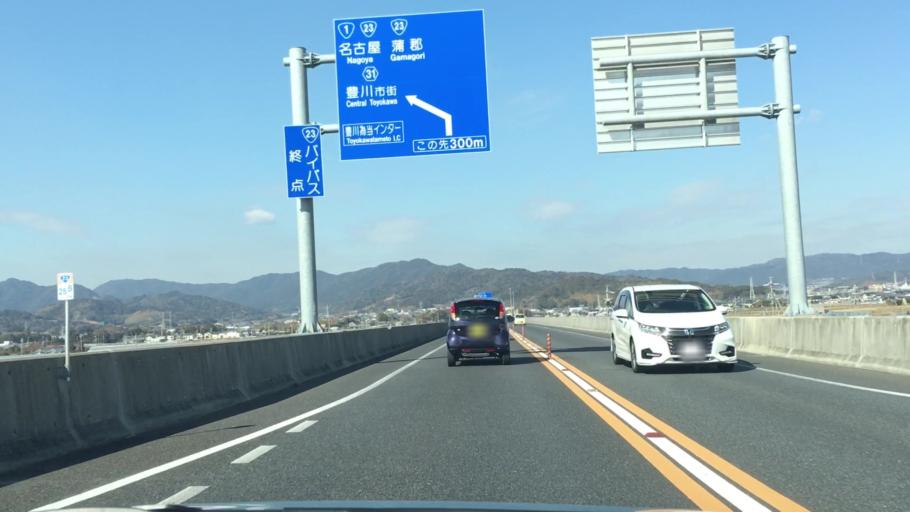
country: JP
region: Aichi
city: Kozakai-cho
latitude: 34.8136
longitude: 137.3328
